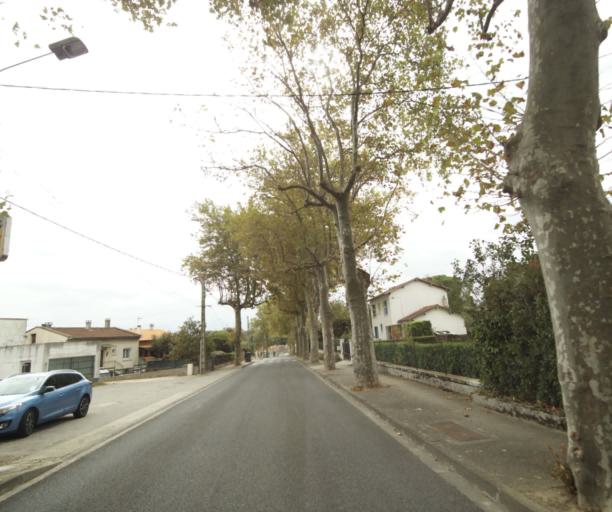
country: FR
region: Midi-Pyrenees
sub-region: Departement de la Haute-Garonne
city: Villefranche-de-Lauragais
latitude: 43.4068
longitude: 1.7173
